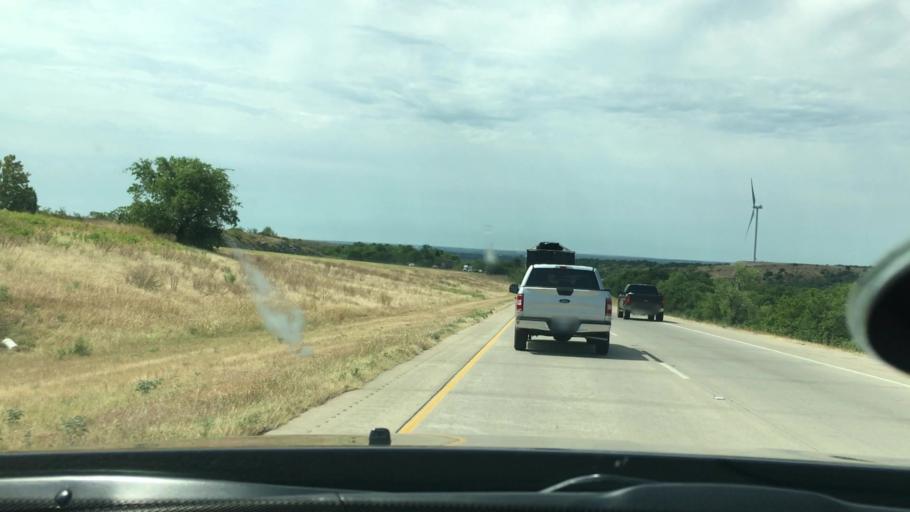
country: US
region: Oklahoma
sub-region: Murray County
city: Davis
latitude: 34.3698
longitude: -97.1465
